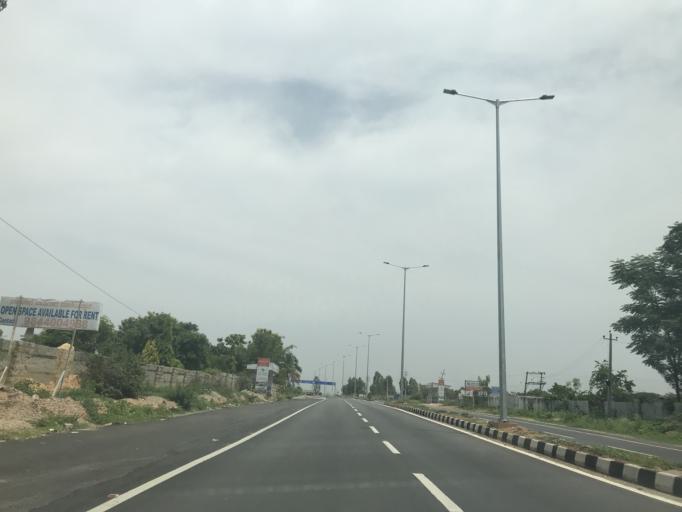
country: IN
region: Karnataka
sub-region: Bangalore Urban
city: Yelahanka
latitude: 13.1210
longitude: 77.6684
